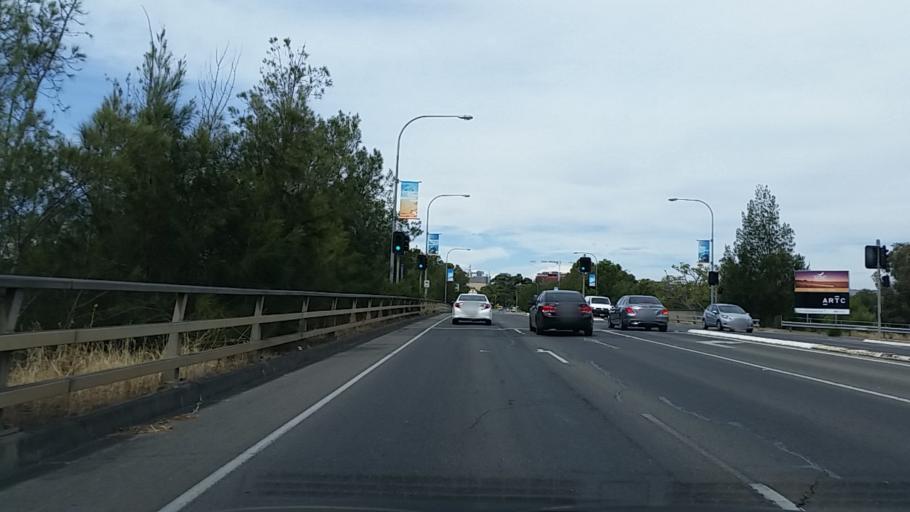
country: AU
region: South Australia
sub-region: Adelaide
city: Adelaide
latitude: -34.9304
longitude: 138.5799
